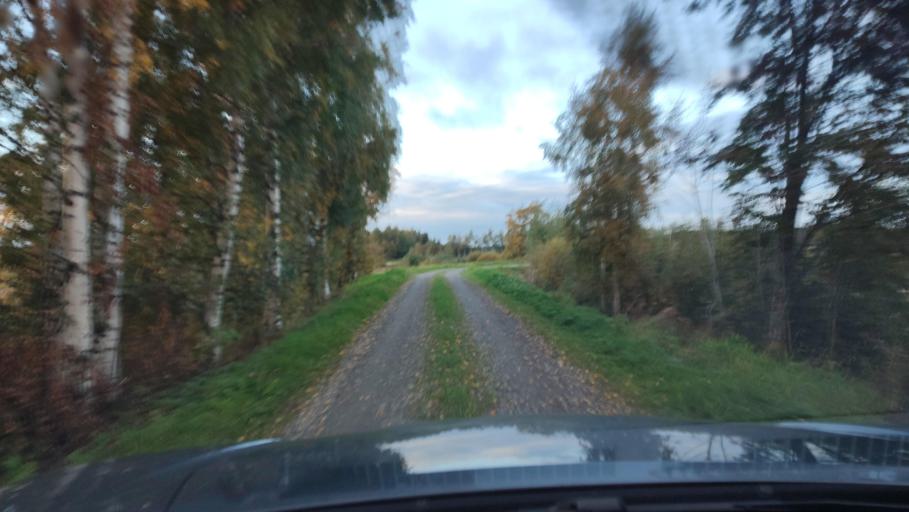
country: FI
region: Ostrobothnia
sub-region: Sydosterbotten
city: Kristinestad
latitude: 62.2375
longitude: 21.4504
